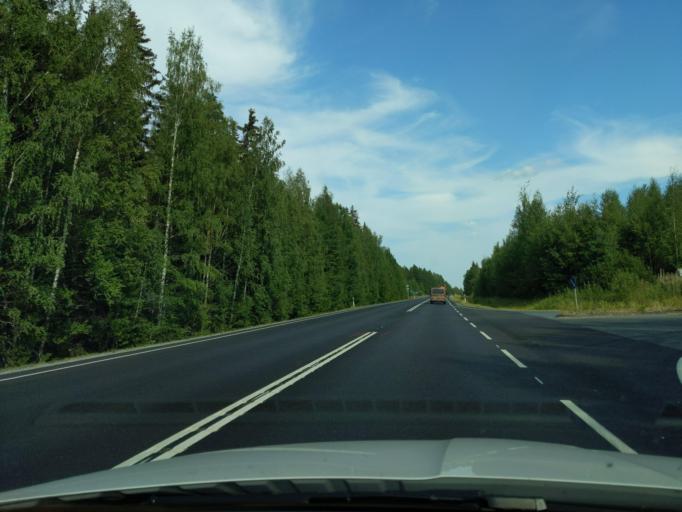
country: FI
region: Haeme
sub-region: Haemeenlinna
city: Hauho
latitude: 61.1729
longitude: 24.6054
